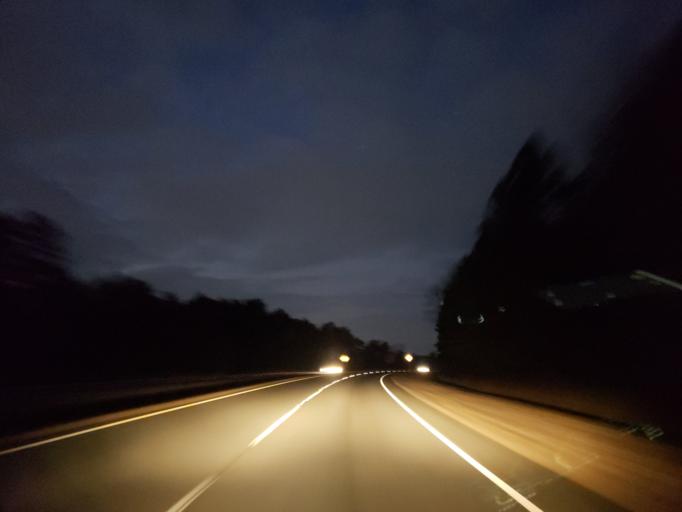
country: US
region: Georgia
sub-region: Polk County
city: Rockmart
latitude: 33.9919
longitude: -85.0249
